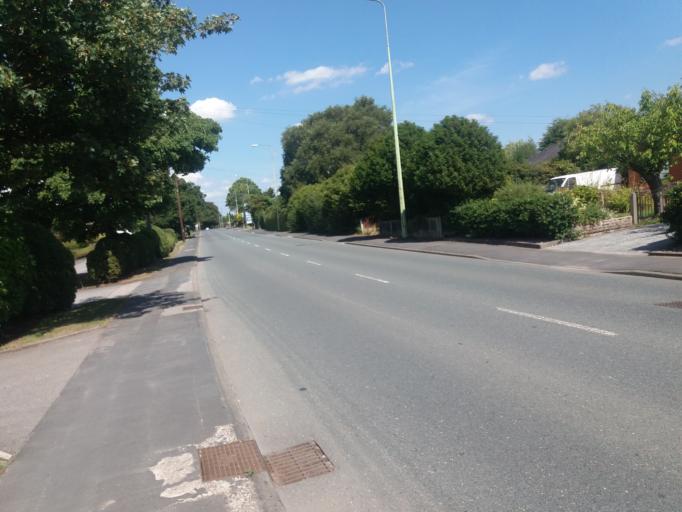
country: GB
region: England
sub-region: Lancashire
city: Euxton
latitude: 53.6727
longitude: -2.6772
